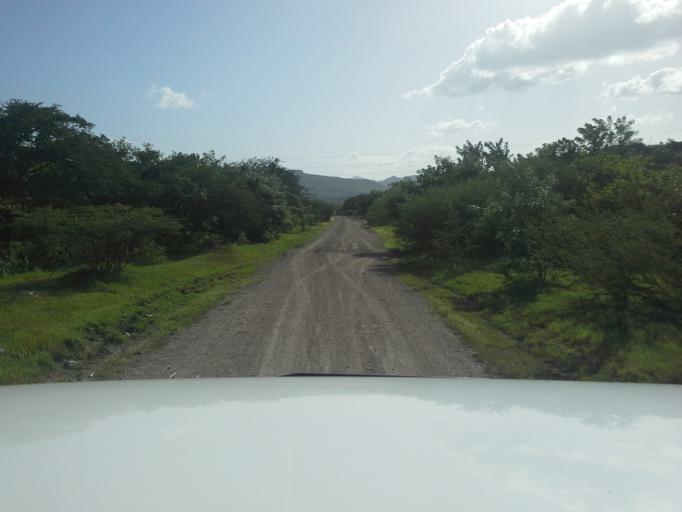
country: NI
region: Matagalpa
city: Ciudad Dario
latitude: 12.6593
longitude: -86.0749
